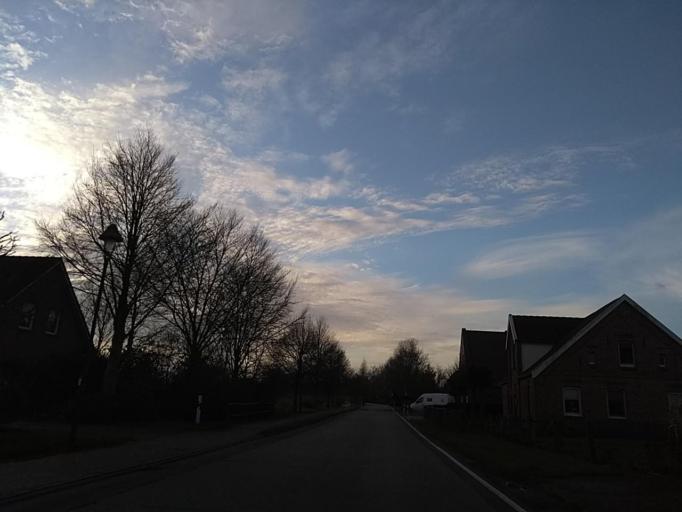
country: DE
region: Lower Saxony
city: Jemgum
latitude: 53.3095
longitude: 7.3139
